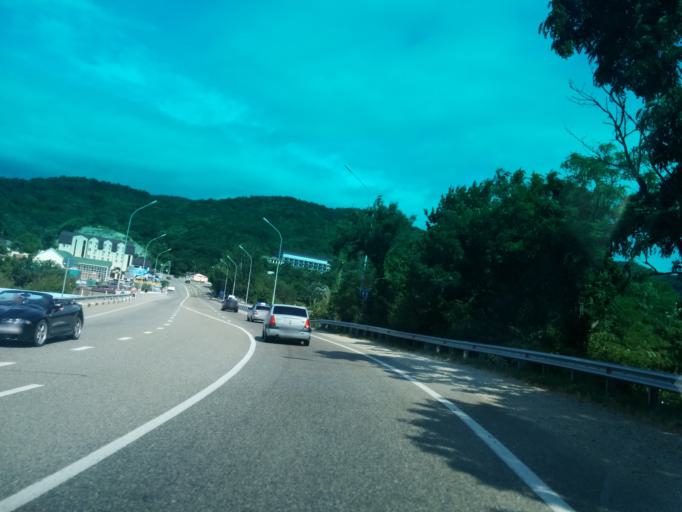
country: RU
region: Krasnodarskiy
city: Nebug
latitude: 44.1645
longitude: 39.0021
